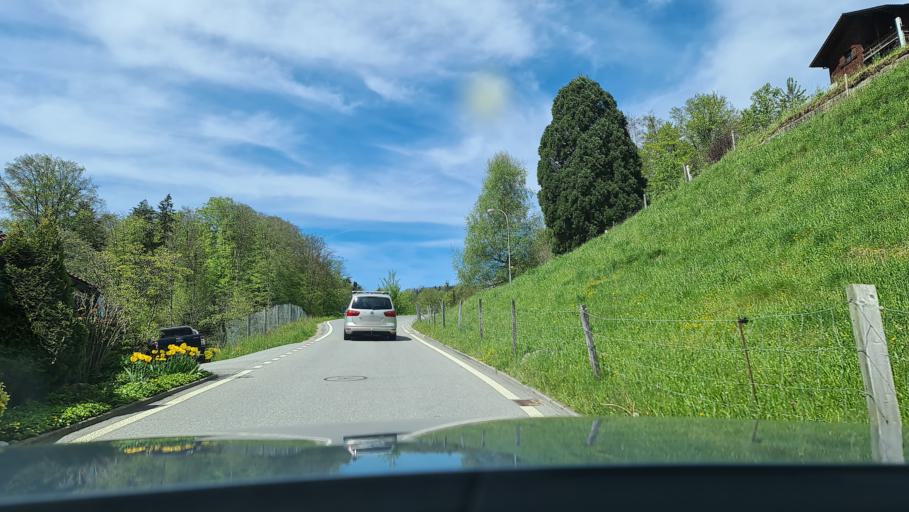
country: CH
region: Lucerne
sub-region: Entlebuch District
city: Werthenstein
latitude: 47.0573
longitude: 8.1000
